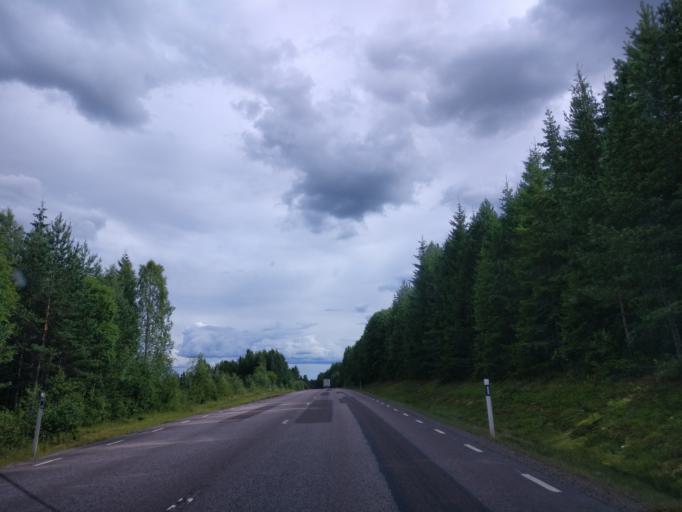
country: SE
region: Vaermland
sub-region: Hagfors Kommun
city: Ekshaerad
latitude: 60.1505
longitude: 13.5194
